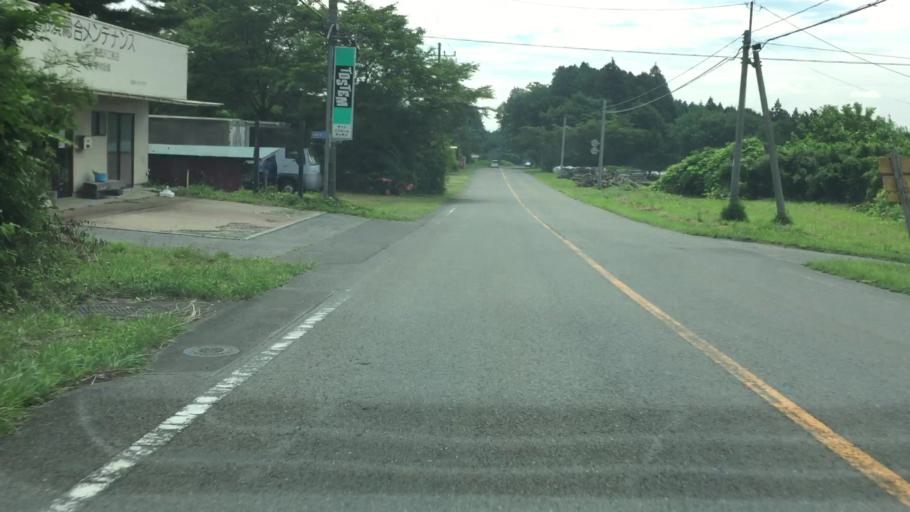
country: JP
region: Tochigi
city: Kuroiso
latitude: 37.0961
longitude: 140.0519
